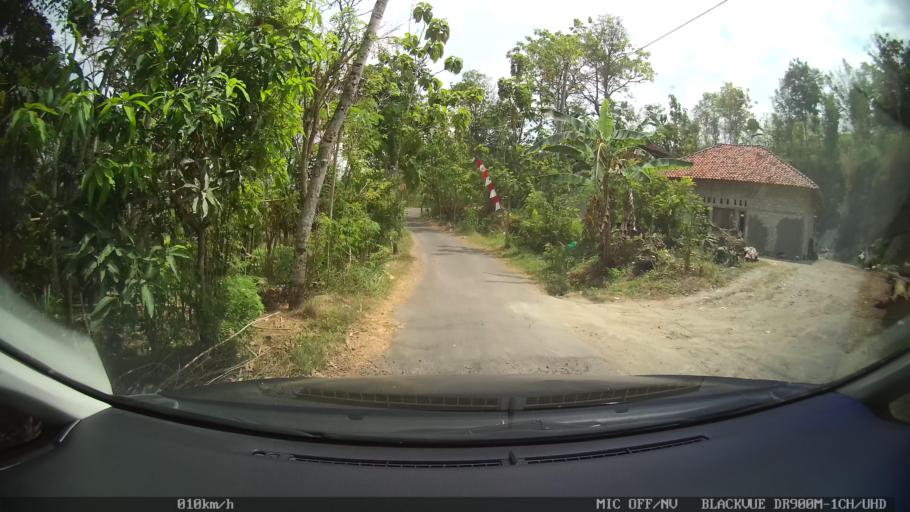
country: ID
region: Central Java
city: Candi Prambanan
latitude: -7.8100
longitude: 110.5224
